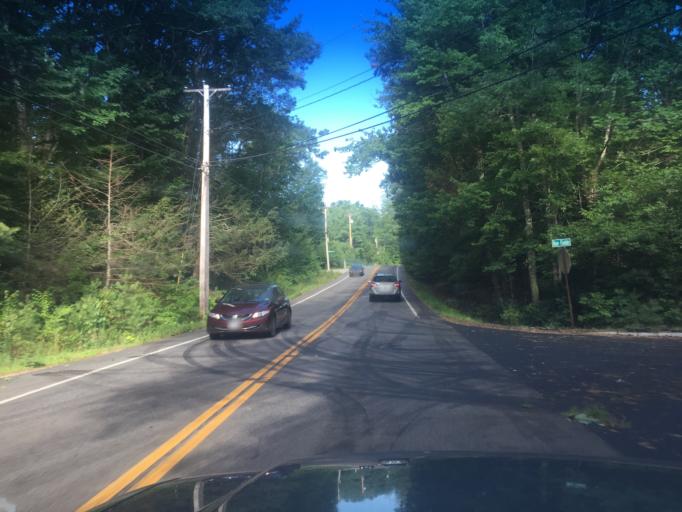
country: US
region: Maine
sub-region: York County
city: South Berwick
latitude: 43.2036
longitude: -70.7720
